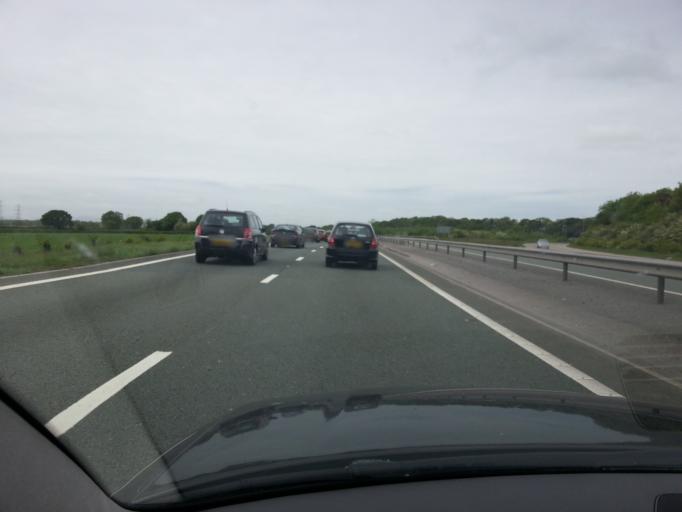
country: GB
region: England
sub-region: Cheshire West and Chester
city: Mollington
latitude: 53.2439
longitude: -2.9322
